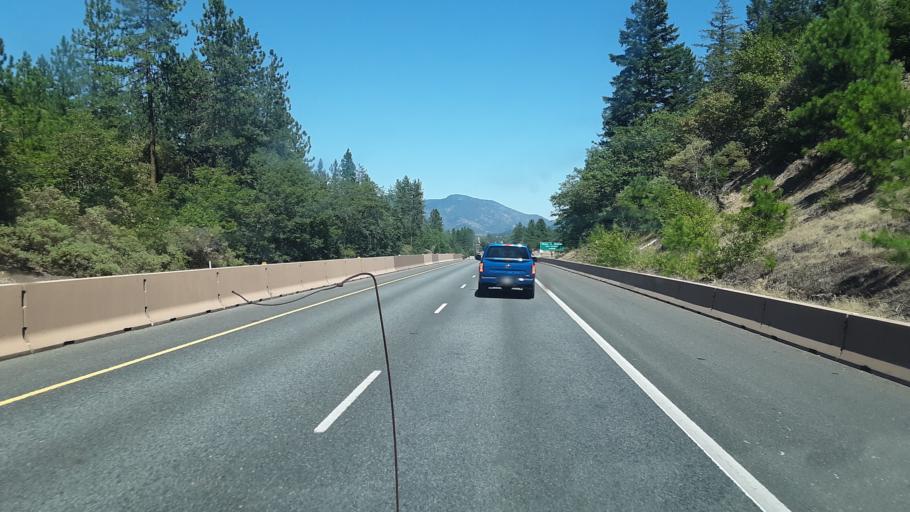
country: US
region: Oregon
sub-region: Josephine County
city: Redwood
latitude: 42.4143
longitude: -123.3964
